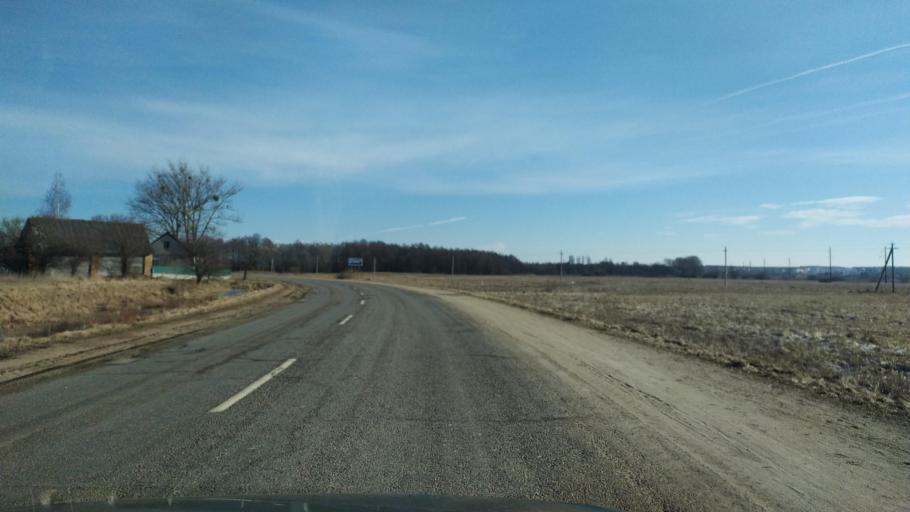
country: BY
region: Brest
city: Kamyanyets
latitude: 52.3985
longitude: 23.7888
